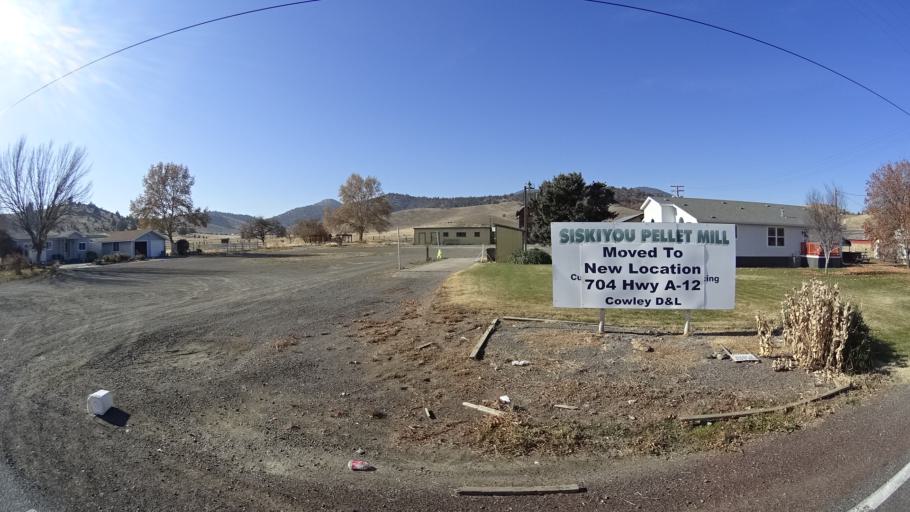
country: US
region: California
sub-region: Siskiyou County
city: Montague
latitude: 41.6456
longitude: -122.5379
